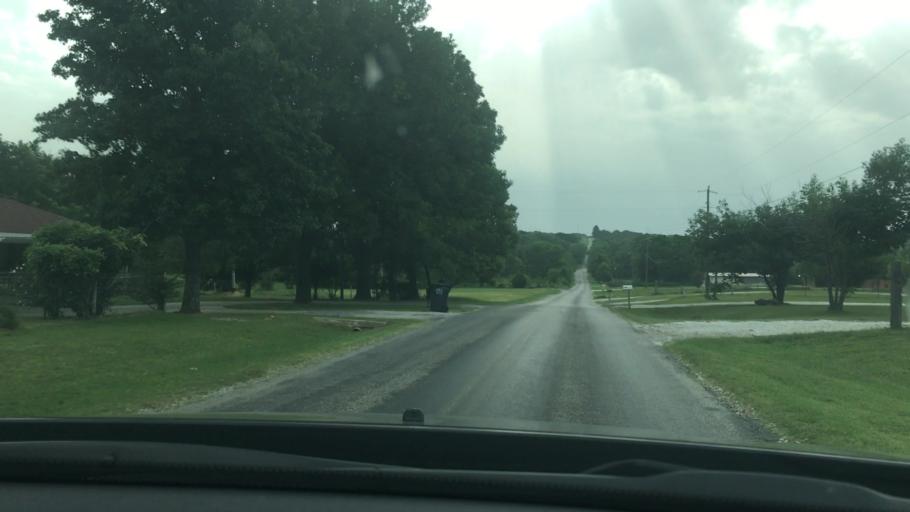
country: US
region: Oklahoma
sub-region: Pontotoc County
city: Ada
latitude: 34.8107
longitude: -96.6504
